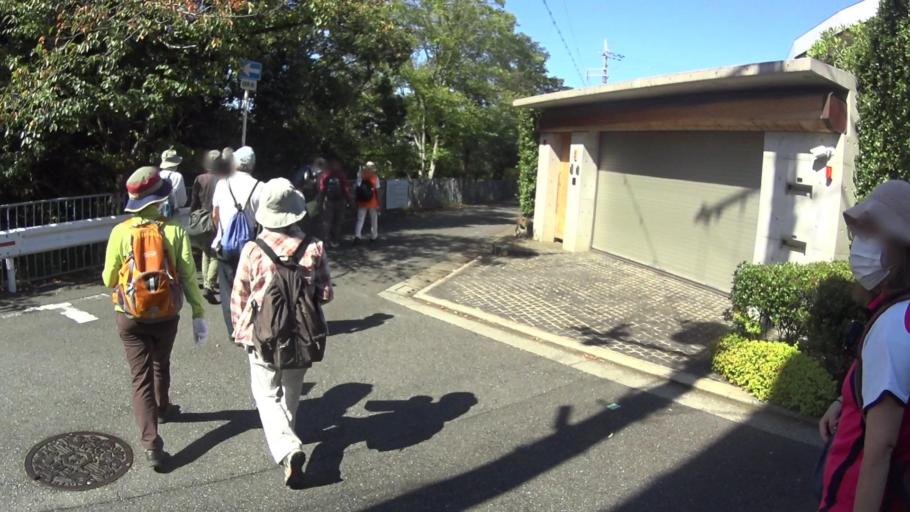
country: JP
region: Osaka
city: Takaishi
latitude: 34.5350
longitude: 135.4669
